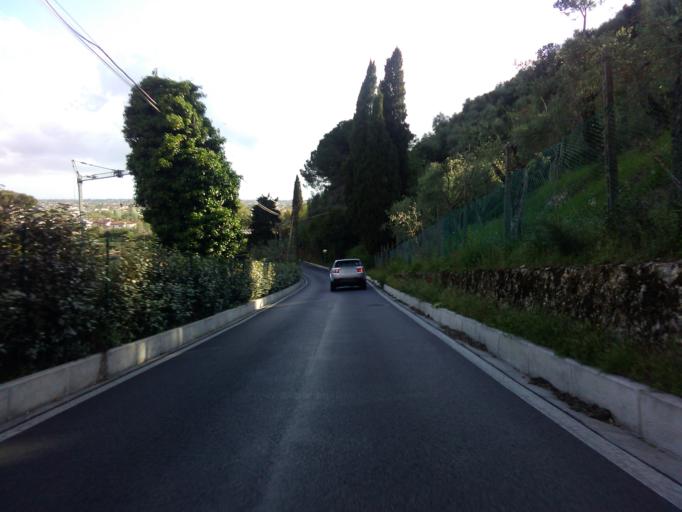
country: IT
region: Tuscany
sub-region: Provincia di Lucca
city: Camaiore
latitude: 43.9396
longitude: 10.2551
